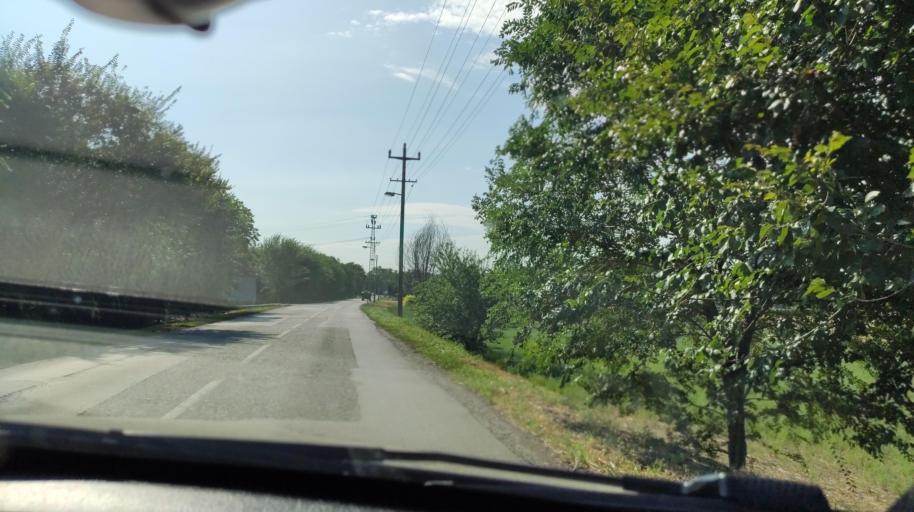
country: RS
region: Autonomna Pokrajina Vojvodina
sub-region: Severnobacki Okrug
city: Backa Topola
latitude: 45.8138
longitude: 19.6195
